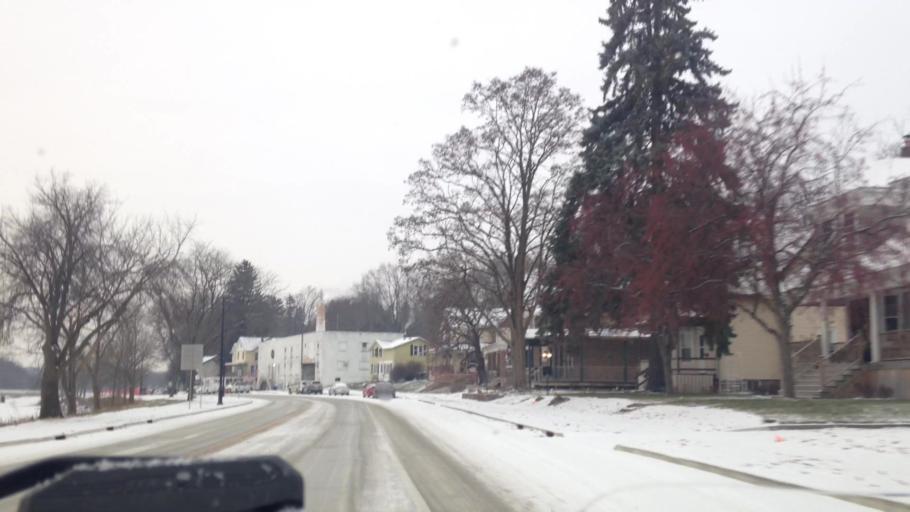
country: US
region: Wisconsin
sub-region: Dodge County
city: Mayville
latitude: 43.4928
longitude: -88.5446
